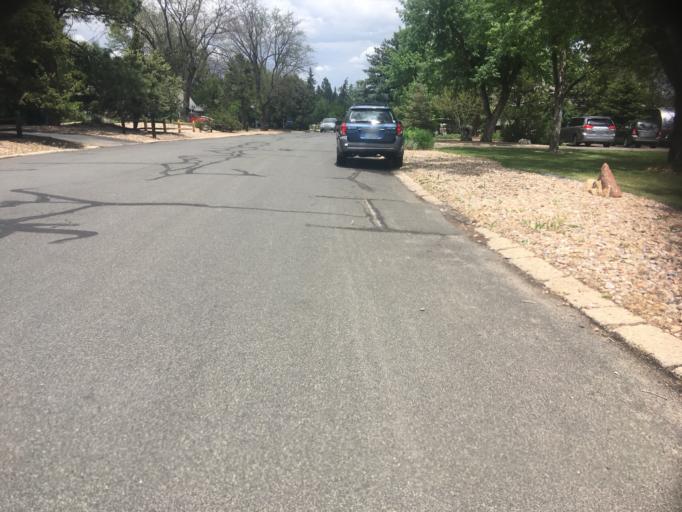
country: US
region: Colorado
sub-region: Boulder County
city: Boulder
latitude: 40.0043
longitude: -105.2328
